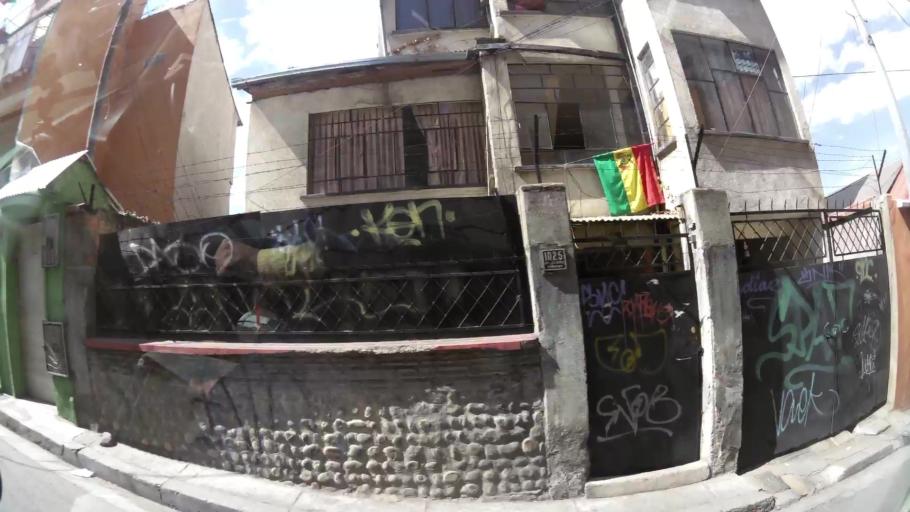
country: BO
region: La Paz
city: La Paz
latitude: -16.4898
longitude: -68.1254
